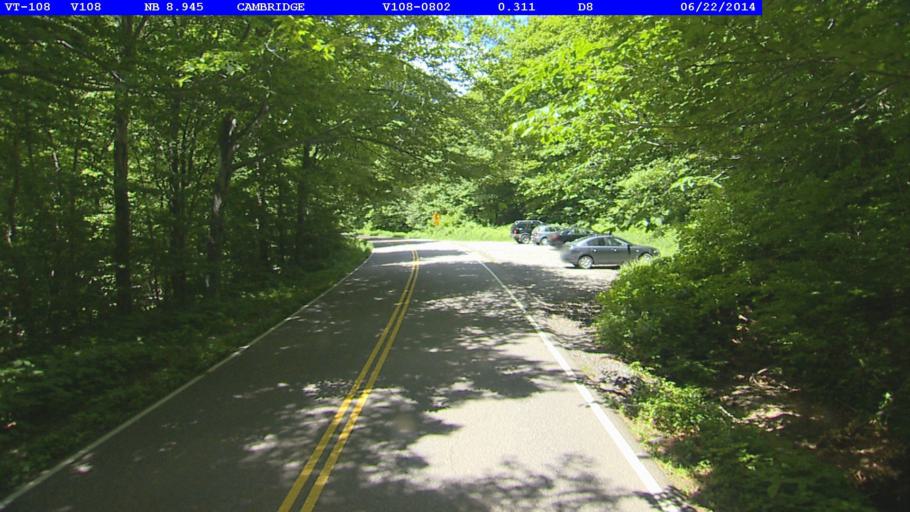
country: US
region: Vermont
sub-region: Lamoille County
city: Johnson
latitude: 44.5471
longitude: -72.7929
